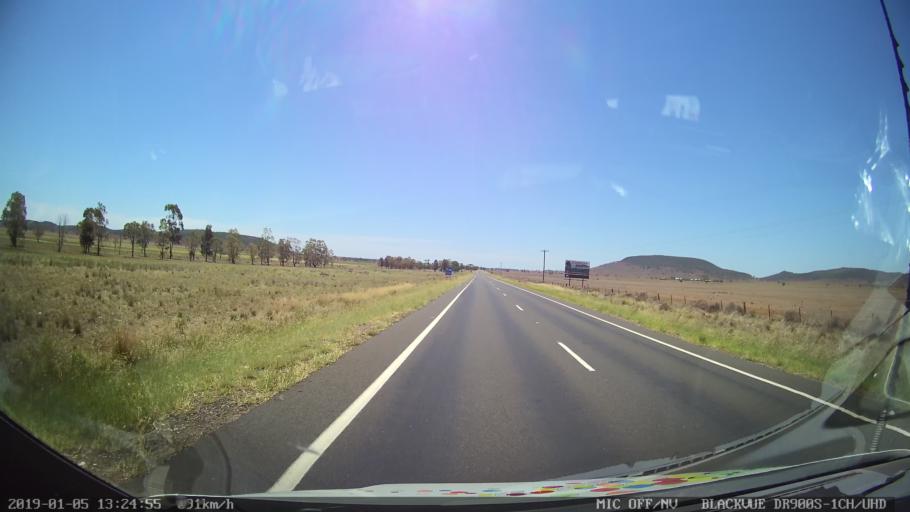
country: AU
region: New South Wales
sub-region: Gunnedah
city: Gunnedah
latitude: -31.0656
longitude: 149.9953
